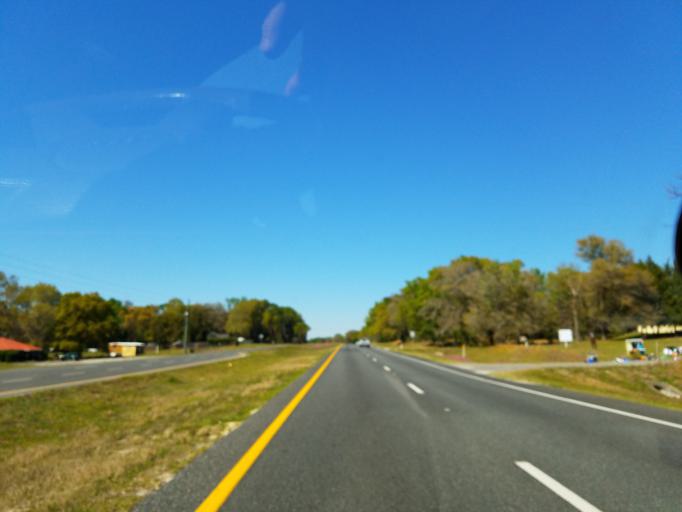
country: US
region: Florida
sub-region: Marion County
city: Belleview
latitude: 29.0303
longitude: -82.0448
